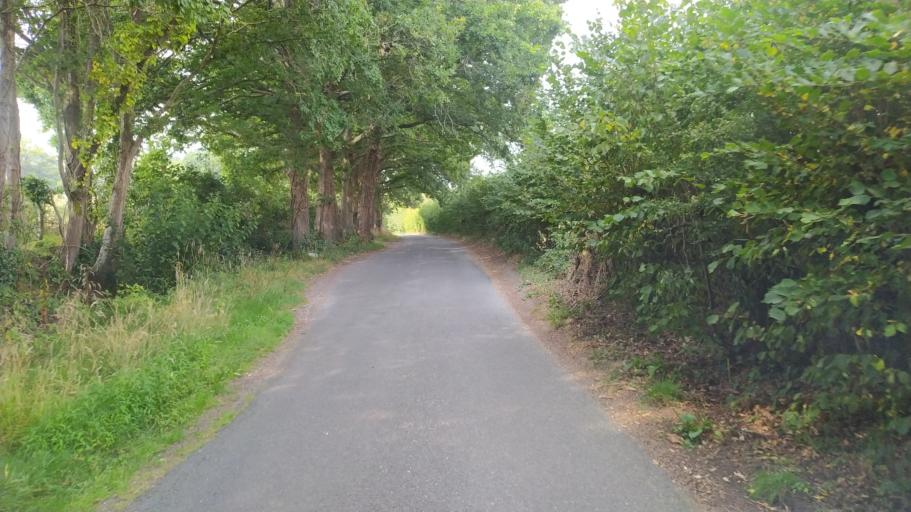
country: GB
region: England
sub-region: Hampshire
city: Romsey
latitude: 50.9960
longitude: -1.4526
